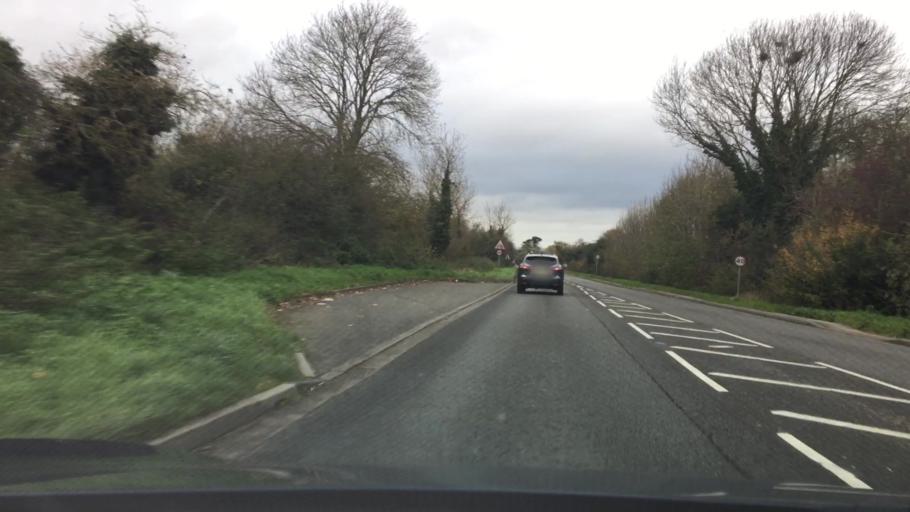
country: GB
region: England
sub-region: Nottinghamshire
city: Lowdham
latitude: 52.9908
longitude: -0.9899
